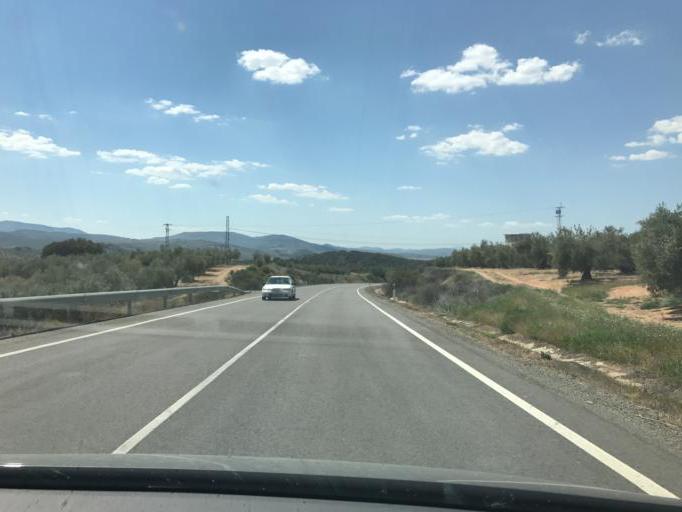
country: ES
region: Andalusia
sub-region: Provincia de Jaen
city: Frailes
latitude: 37.4284
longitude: -3.7920
